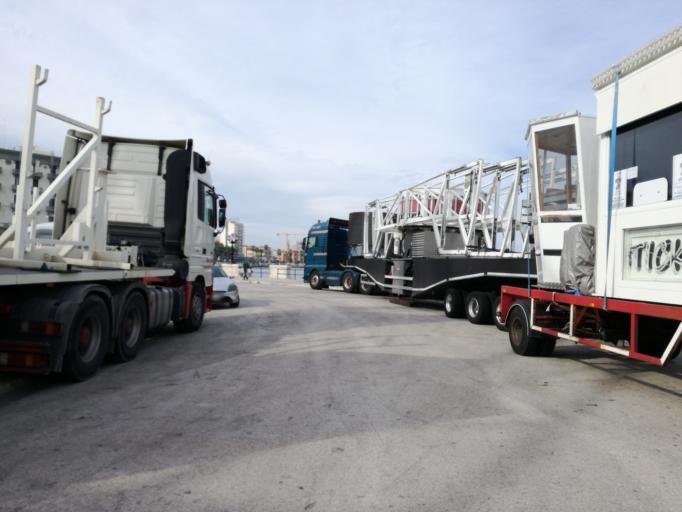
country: IT
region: Apulia
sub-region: Provincia di Bari
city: Bari
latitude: 41.1229
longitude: 16.8788
